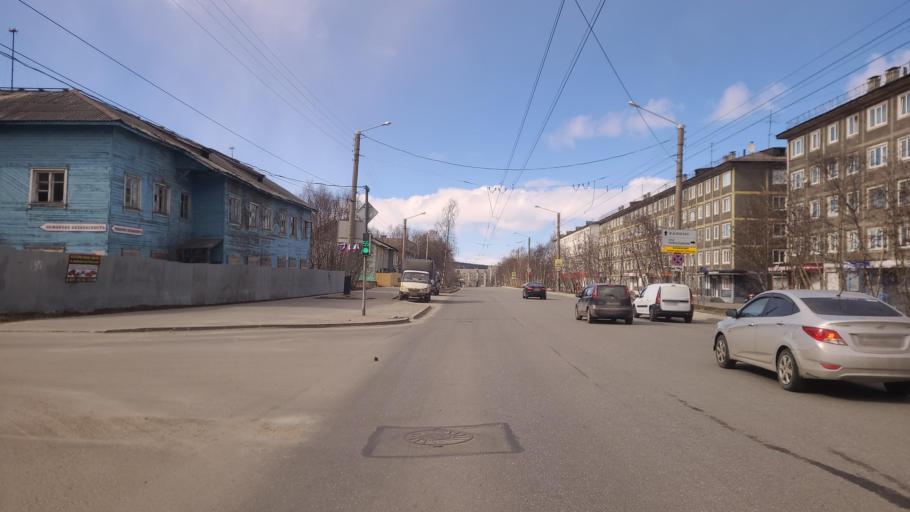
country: RU
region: Murmansk
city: Murmansk
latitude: 68.9521
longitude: 33.0727
